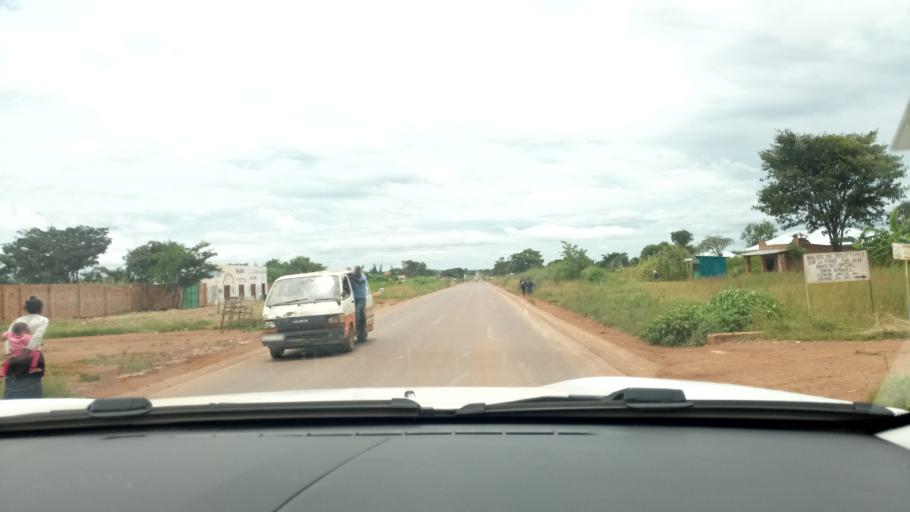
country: CD
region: Katanga
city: Lubumbashi
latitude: -11.5704
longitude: 27.5468
